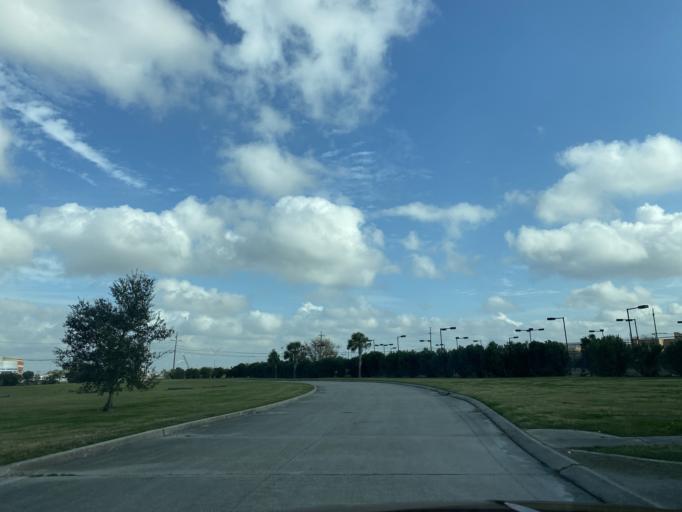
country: US
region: Louisiana
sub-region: Orleans Parish
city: New Orleans
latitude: 30.0294
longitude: -90.0478
